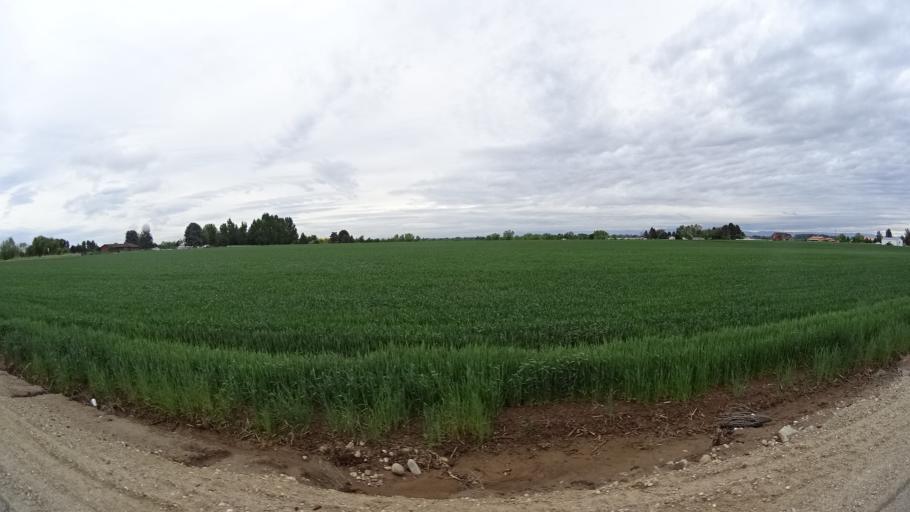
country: US
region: Idaho
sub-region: Ada County
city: Star
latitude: 43.7176
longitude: -116.4843
